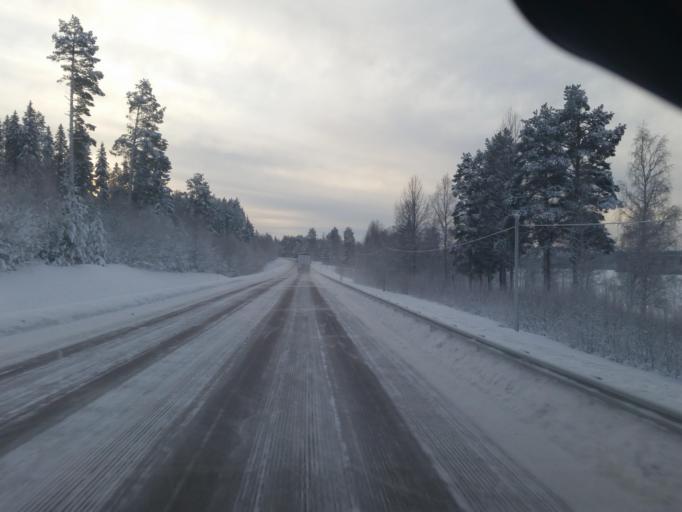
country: SE
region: Norrbotten
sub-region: Alvsbyns Kommun
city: AElvsbyn
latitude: 65.6656
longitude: 21.2192
